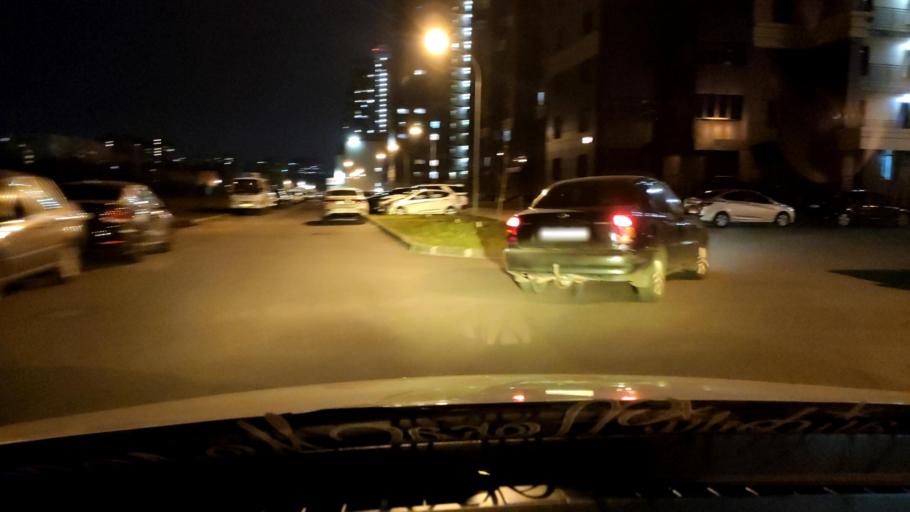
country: RU
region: Voronezj
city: Podgornoye
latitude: 51.7204
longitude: 39.1823
